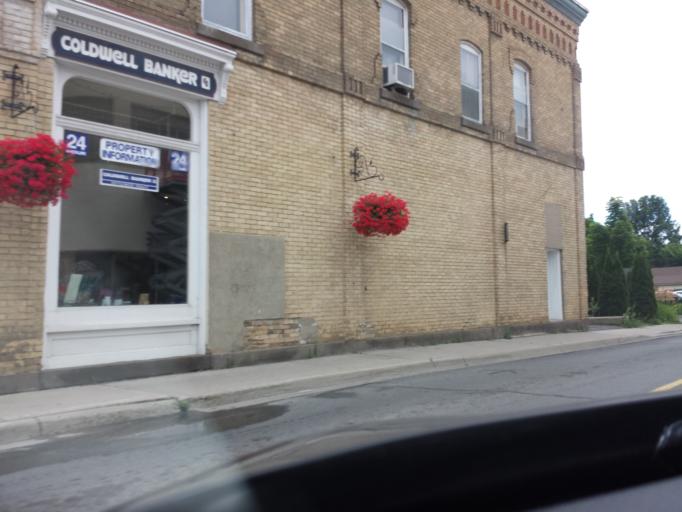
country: CA
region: Ontario
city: Perth
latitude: 44.9004
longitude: -76.2527
